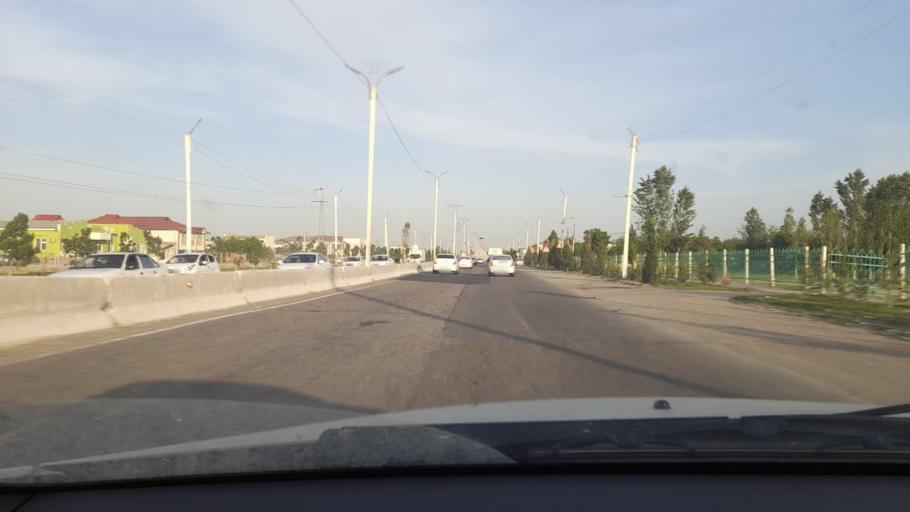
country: KZ
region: Ongtustik Qazaqstan
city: Myrzakent
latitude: 40.5487
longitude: 68.4053
